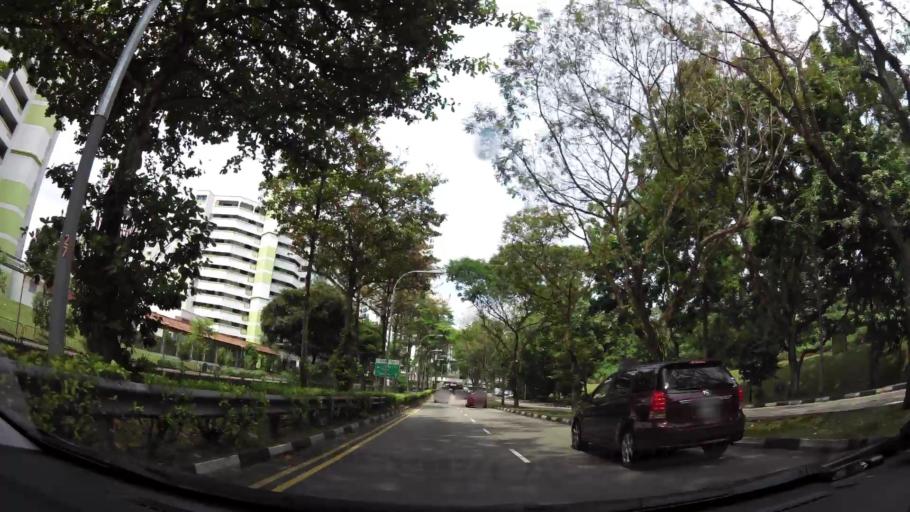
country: SG
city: Singapore
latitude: 1.3505
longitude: 103.7605
